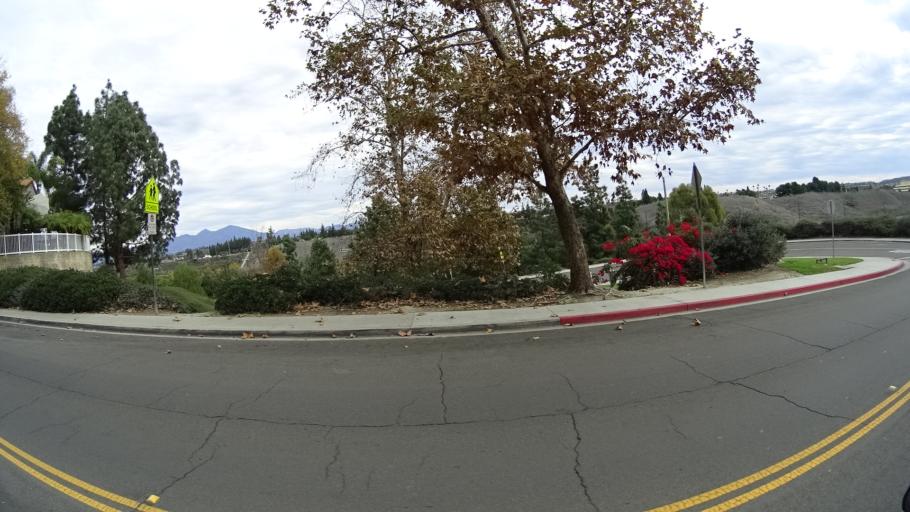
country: US
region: California
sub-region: Orange County
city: Aliso Viejo
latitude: 33.5675
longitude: -117.7199
